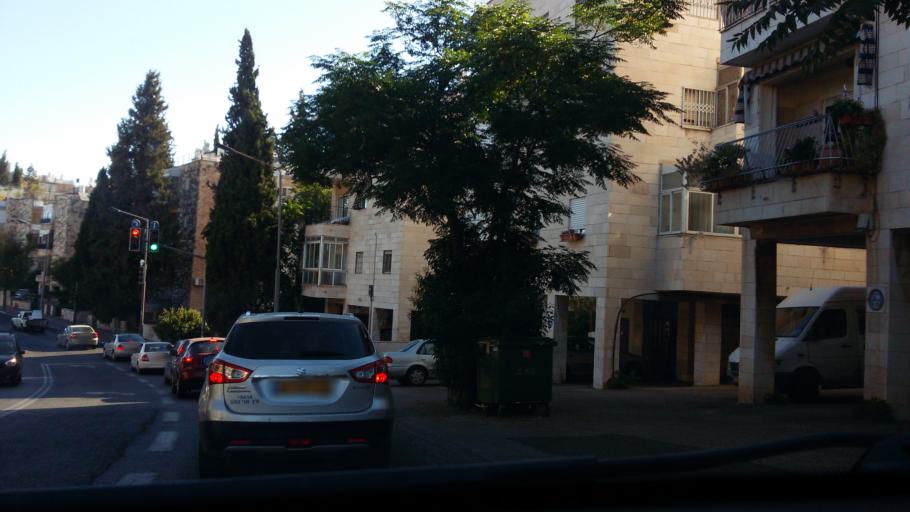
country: IL
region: Jerusalem
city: Jerusalem
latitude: 31.7643
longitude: 35.2059
